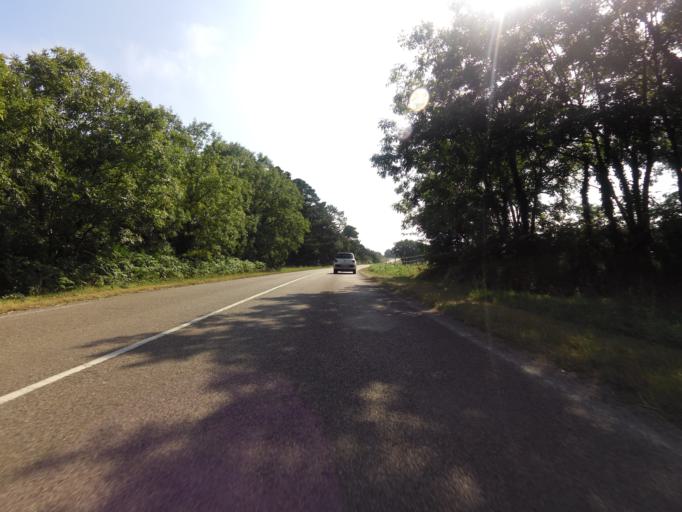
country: FR
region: Brittany
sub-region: Departement du Finistere
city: Plouhinec
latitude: 48.0121
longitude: -4.4702
